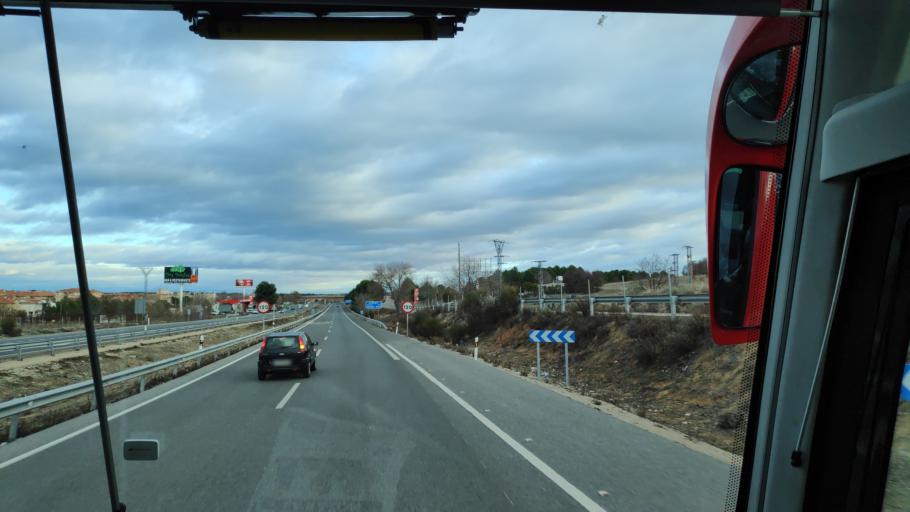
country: ES
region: Madrid
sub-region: Provincia de Madrid
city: Villarejo de Salvanes
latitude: 40.1690
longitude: -3.2889
